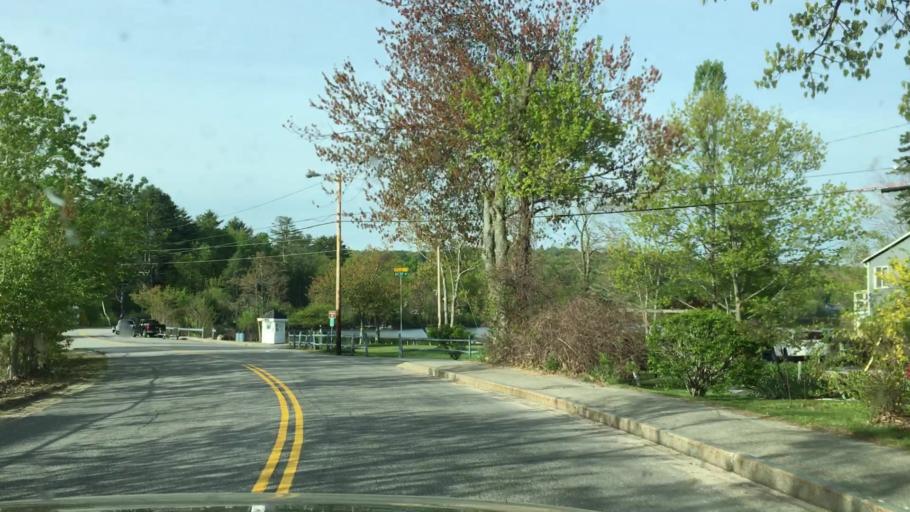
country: US
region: New Hampshire
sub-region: Belknap County
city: Meredith
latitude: 43.6501
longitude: -71.5050
